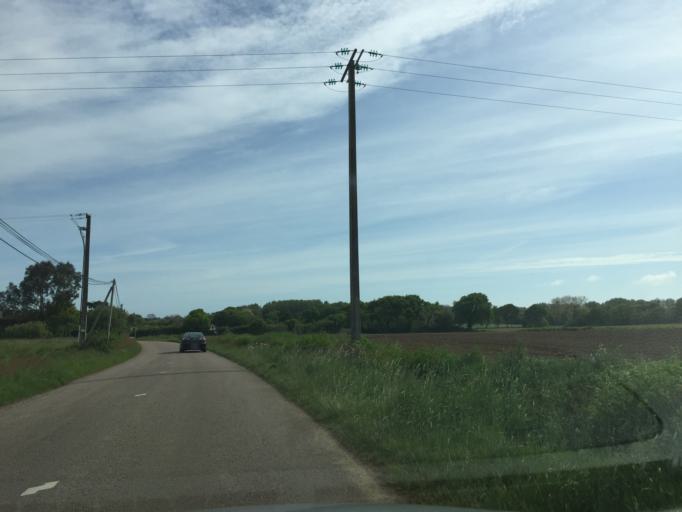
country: FR
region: Brittany
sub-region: Departement des Cotes-d'Armor
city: Matignon
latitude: 48.6568
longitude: -2.3274
